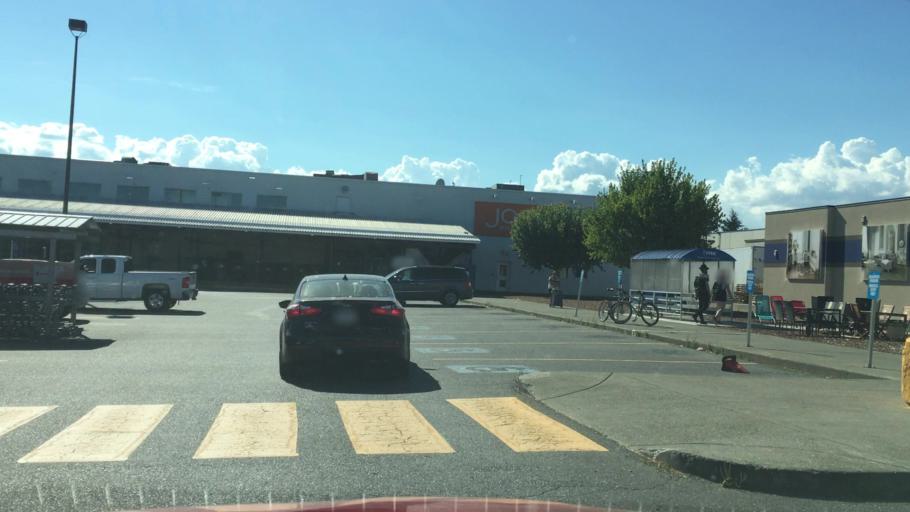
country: CA
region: British Columbia
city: Duncan
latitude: 48.7748
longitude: -123.7027
